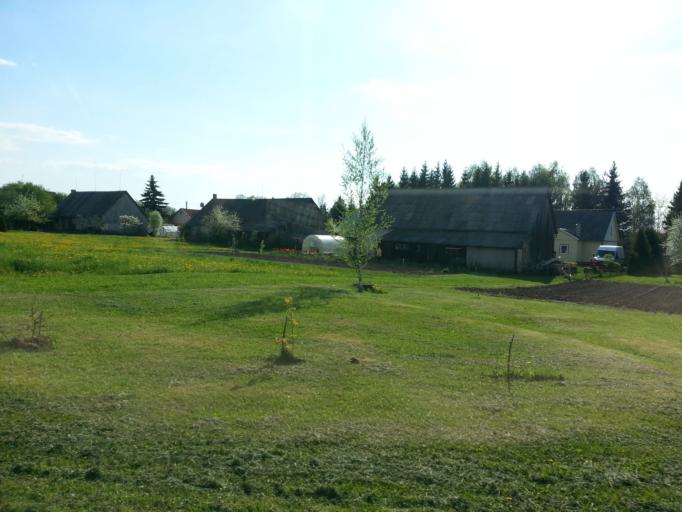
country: LT
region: Panevezys
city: Pasvalys
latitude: 56.0260
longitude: 24.3615
